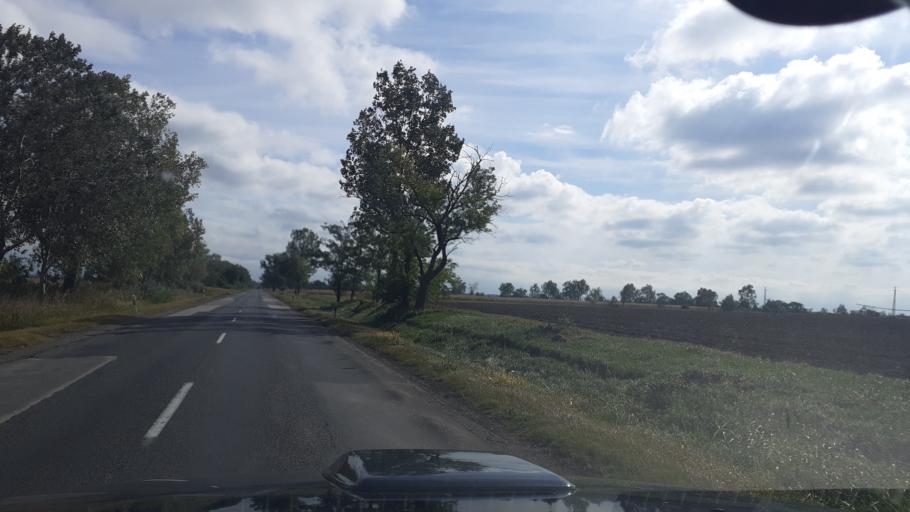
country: HU
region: Bacs-Kiskun
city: Solt
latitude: 46.7981
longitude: 19.0888
